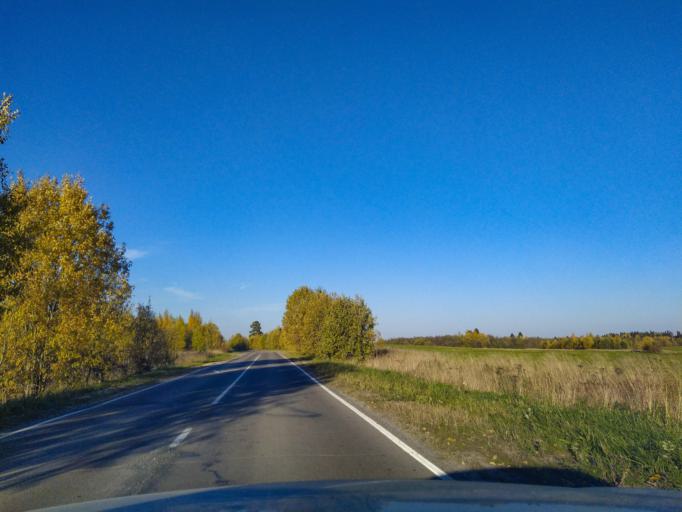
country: RU
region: Leningrad
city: Siverskiy
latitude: 59.3116
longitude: 30.0311
